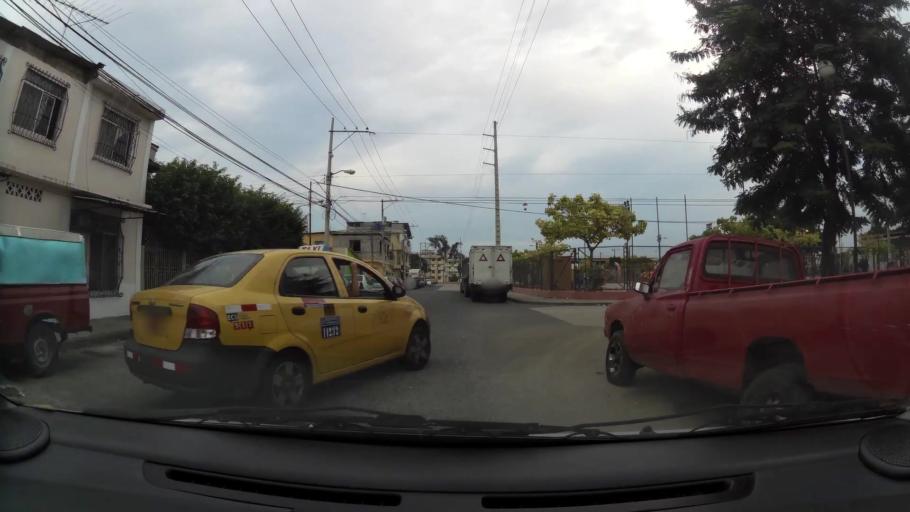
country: EC
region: Guayas
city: Guayaquil
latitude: -2.2382
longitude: -79.8887
